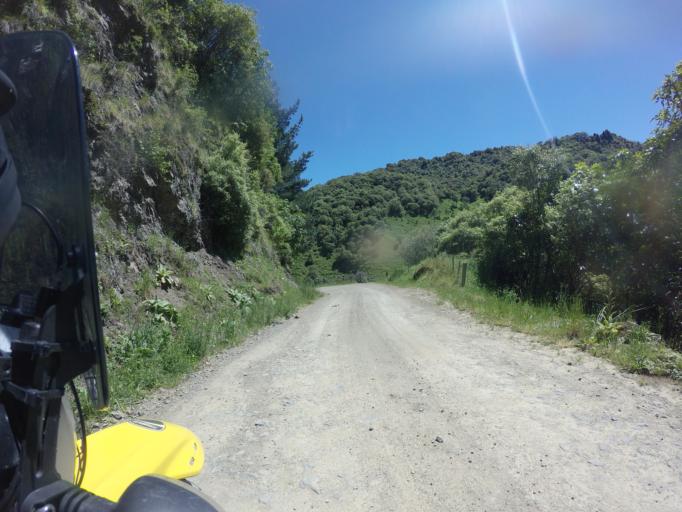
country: NZ
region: Bay of Plenty
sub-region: Opotiki District
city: Opotiki
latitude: -38.4128
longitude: 177.3929
